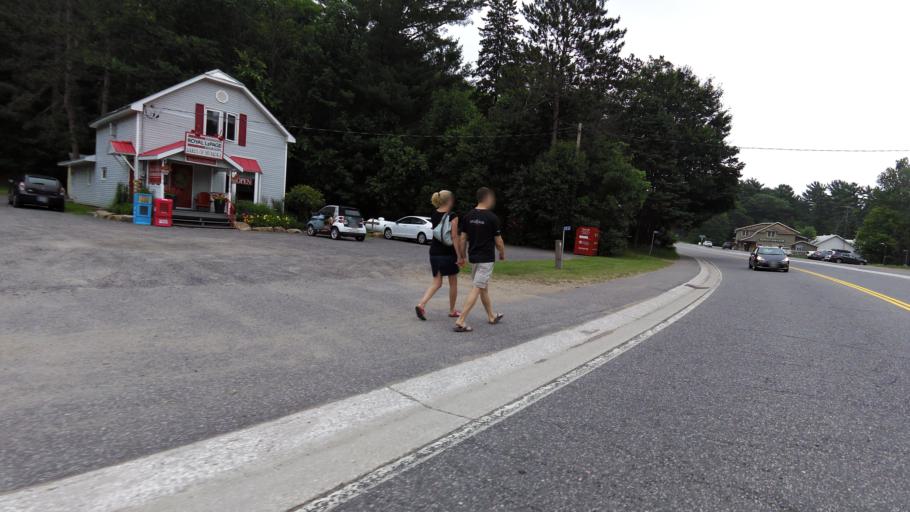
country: CA
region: Ontario
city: Huntsville
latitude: 45.3312
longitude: -79.0134
